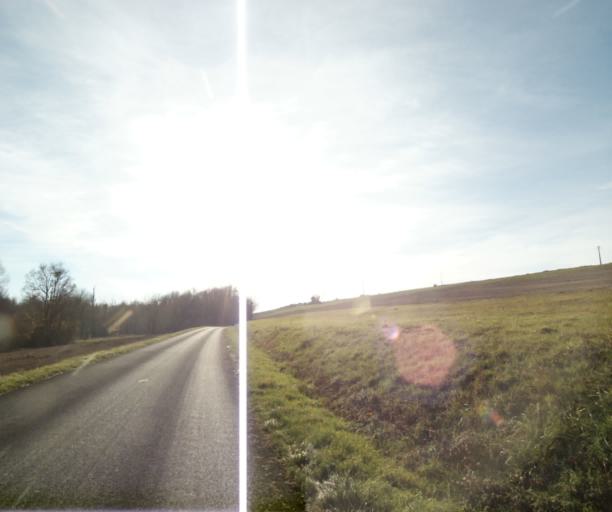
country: FR
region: Poitou-Charentes
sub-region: Departement de la Charente-Maritime
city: Chaniers
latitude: 45.7208
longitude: -0.5213
